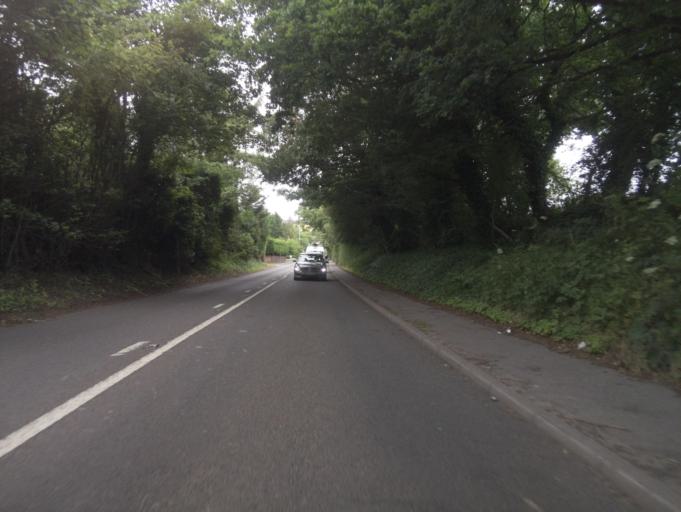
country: GB
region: England
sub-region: Derbyshire
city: Swadlincote
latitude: 52.7961
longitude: -1.5805
